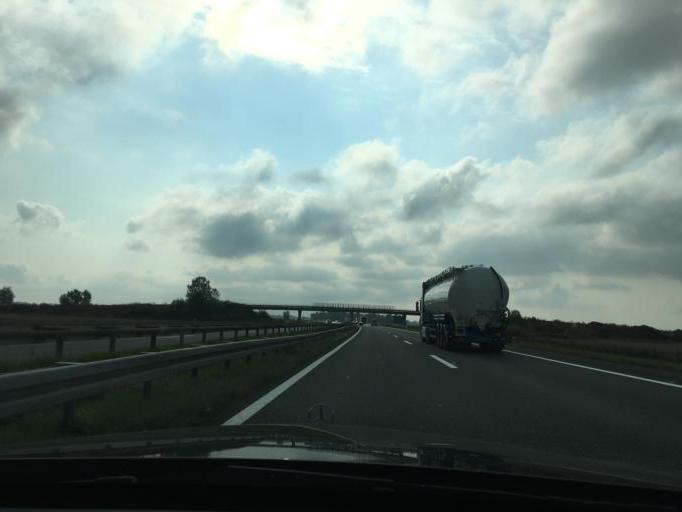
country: HR
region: Sisacko-Moslavacka
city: Osekovo
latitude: 45.5769
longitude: 16.5662
